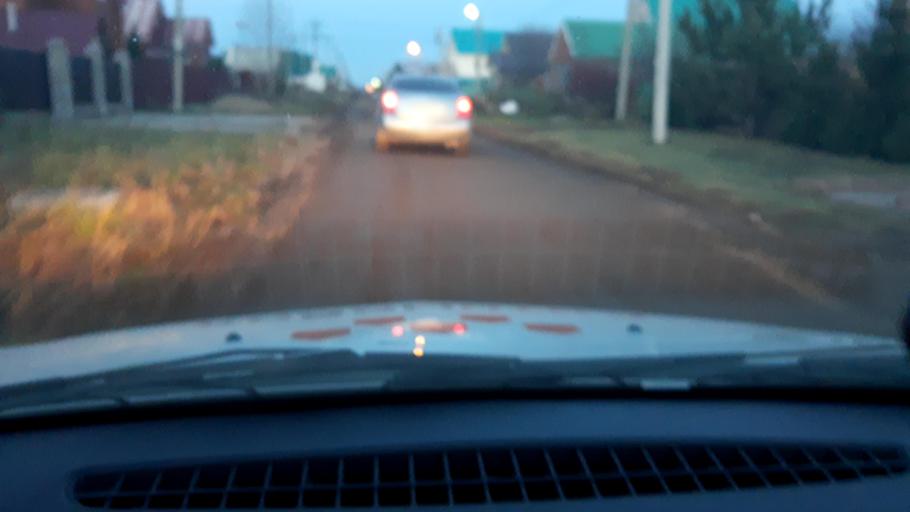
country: RU
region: Bashkortostan
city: Iglino
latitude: 54.7805
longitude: 56.2385
